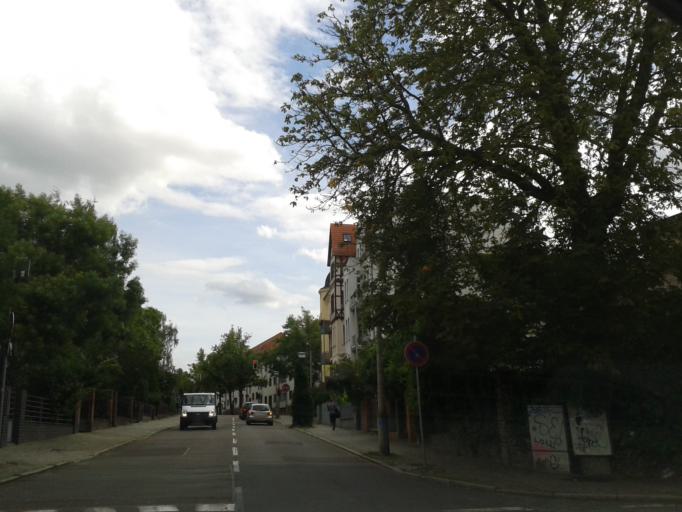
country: DE
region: Saxony-Anhalt
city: Halle (Saale)
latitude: 51.5024
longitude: 11.9687
